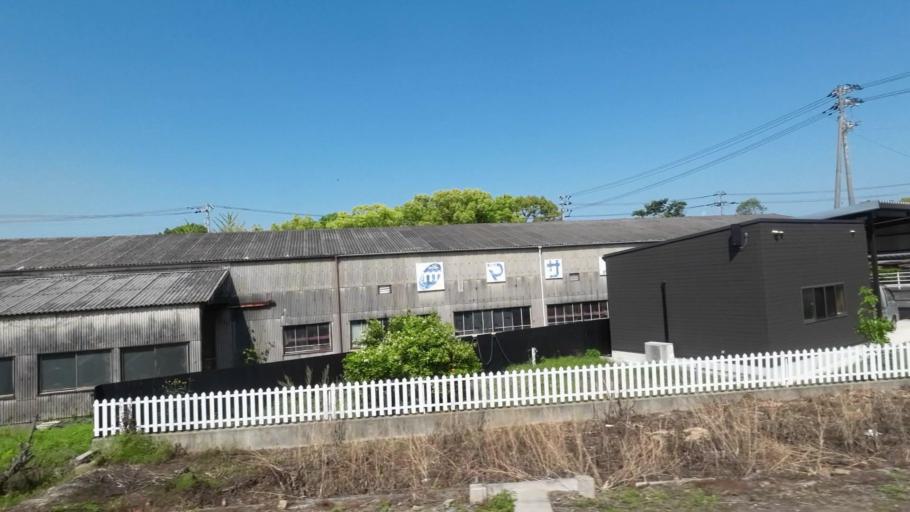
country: JP
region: Ehime
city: Kawanoecho
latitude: 34.0170
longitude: 133.5766
